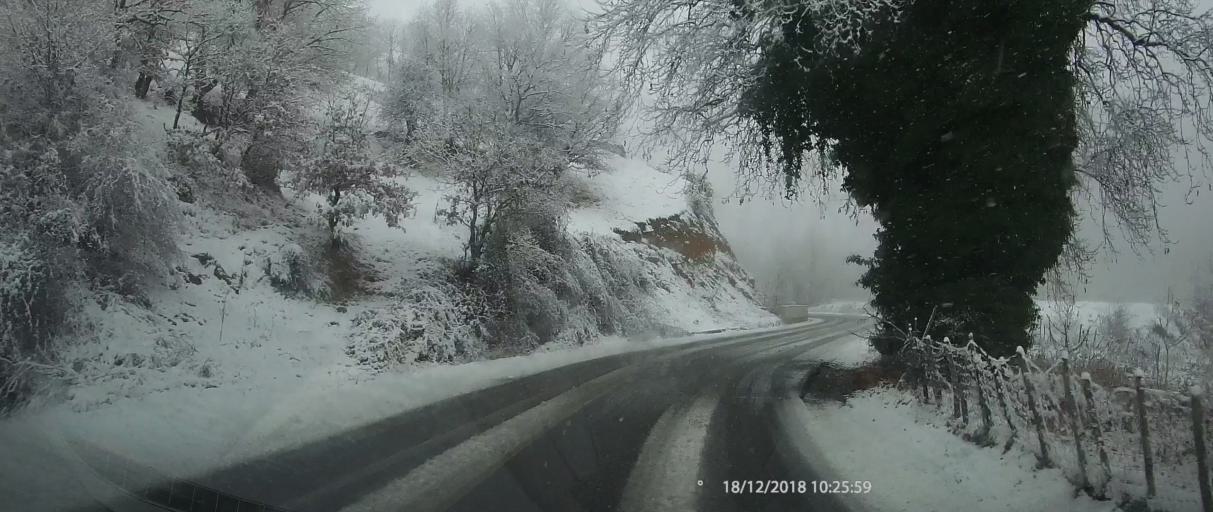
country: GR
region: Thessaly
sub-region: Nomos Larisis
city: Livadi
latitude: 40.1679
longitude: 22.2496
